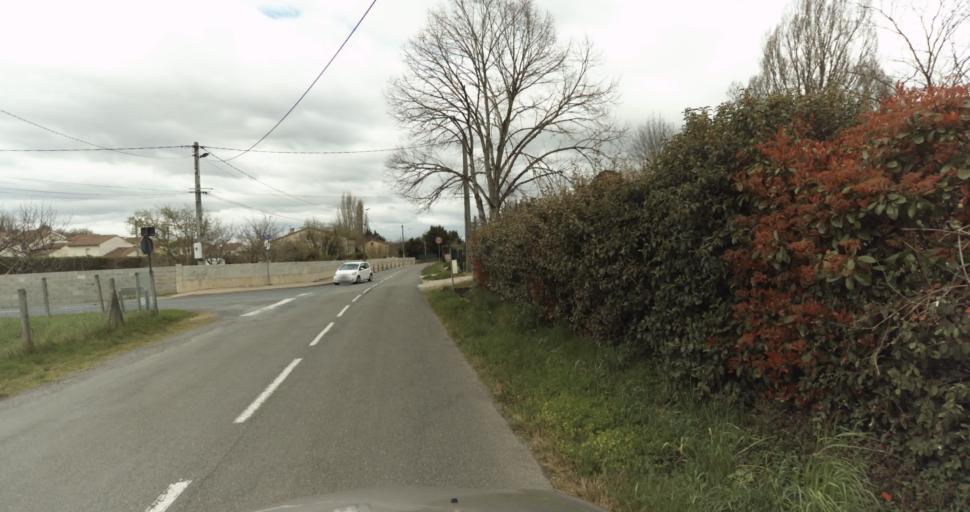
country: FR
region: Midi-Pyrenees
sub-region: Departement du Tarn
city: Puygouzon
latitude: 43.9119
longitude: 2.1686
